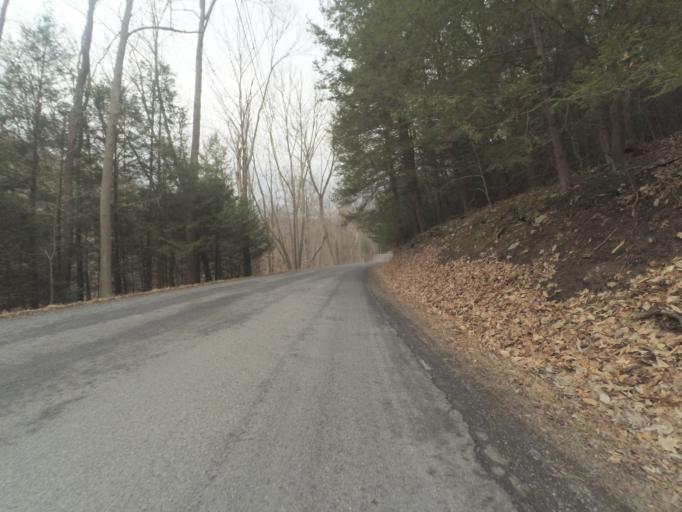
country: US
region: Pennsylvania
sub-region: Centre County
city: Stormstown
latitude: 40.8567
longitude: -78.0134
